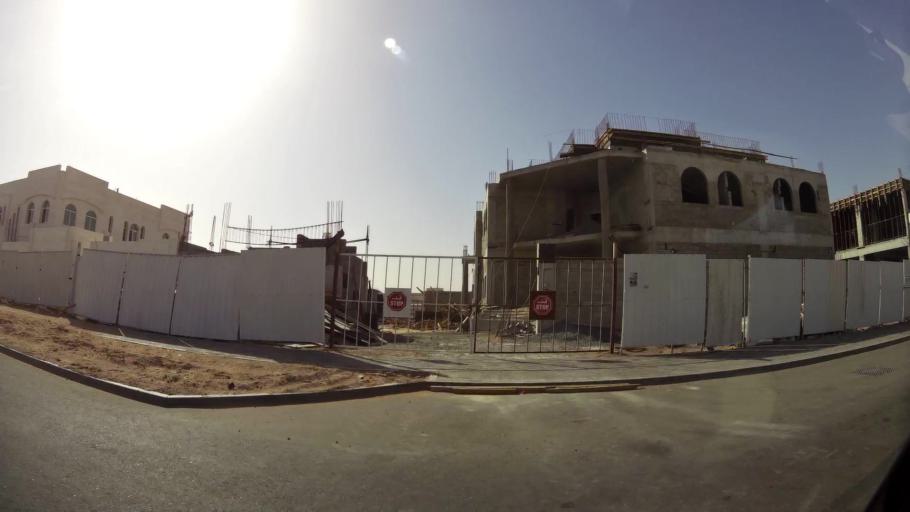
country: OM
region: Al Buraimi
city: Al Buraymi
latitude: 24.3578
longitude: 55.7911
